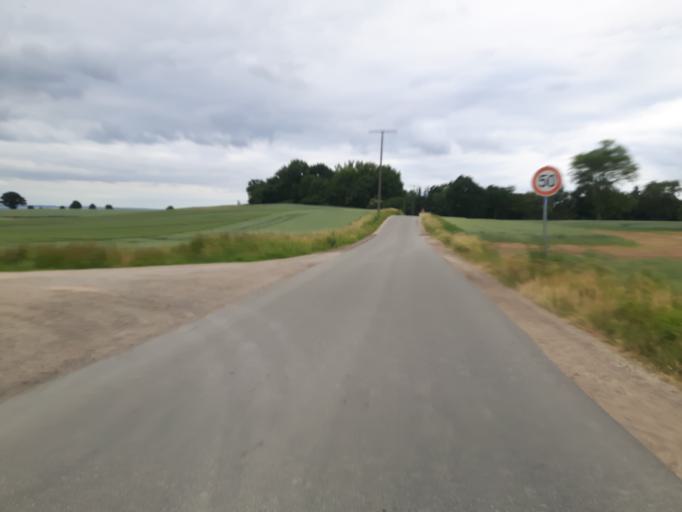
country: DE
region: Schleswig-Holstein
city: Schashagen
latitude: 54.1183
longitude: 10.9047
